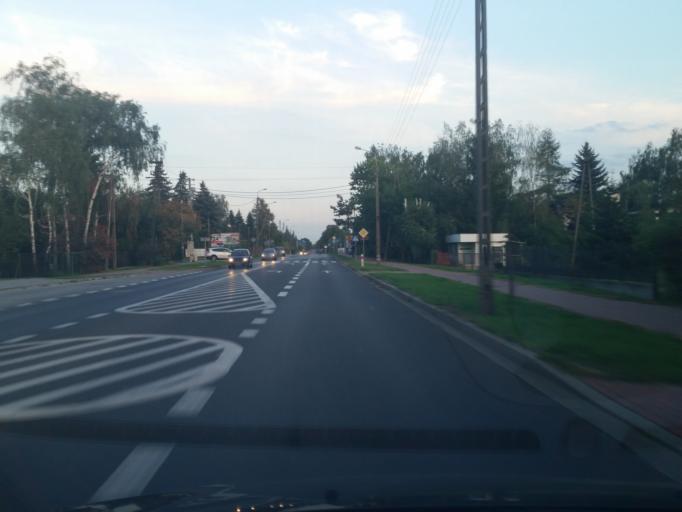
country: PL
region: Masovian Voivodeship
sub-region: Powiat legionowski
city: Jablonna
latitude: 52.3828
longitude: 20.9049
